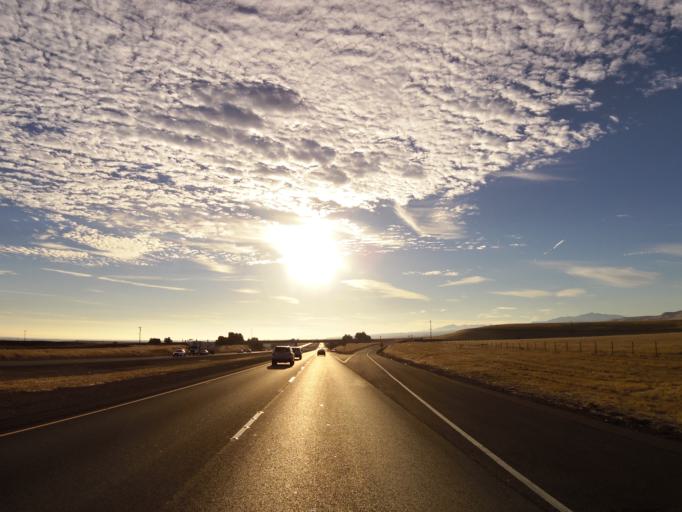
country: US
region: California
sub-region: San Joaquin County
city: Tracy
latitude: 37.6741
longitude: -121.4606
